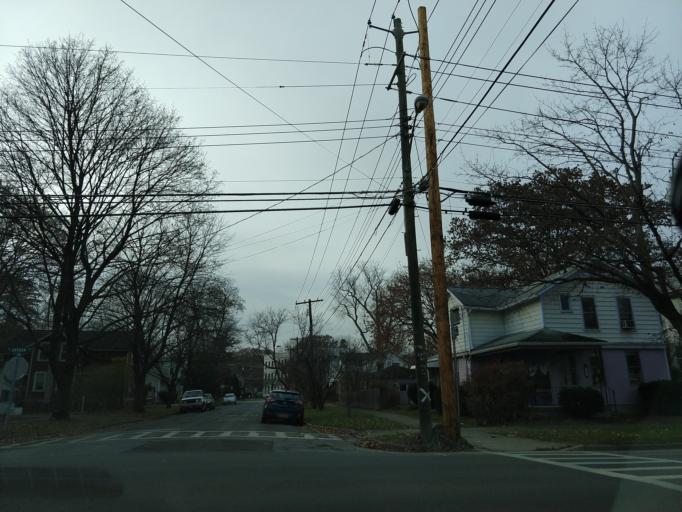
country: US
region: New York
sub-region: Tompkins County
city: Ithaca
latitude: 42.4496
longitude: -76.4995
